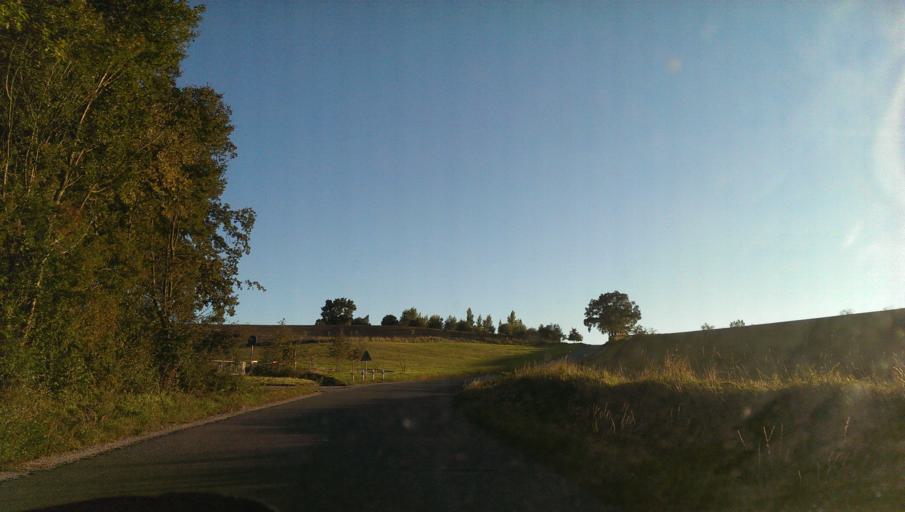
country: CZ
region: Zlin
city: Velehrad
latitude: 49.0990
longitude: 17.3886
